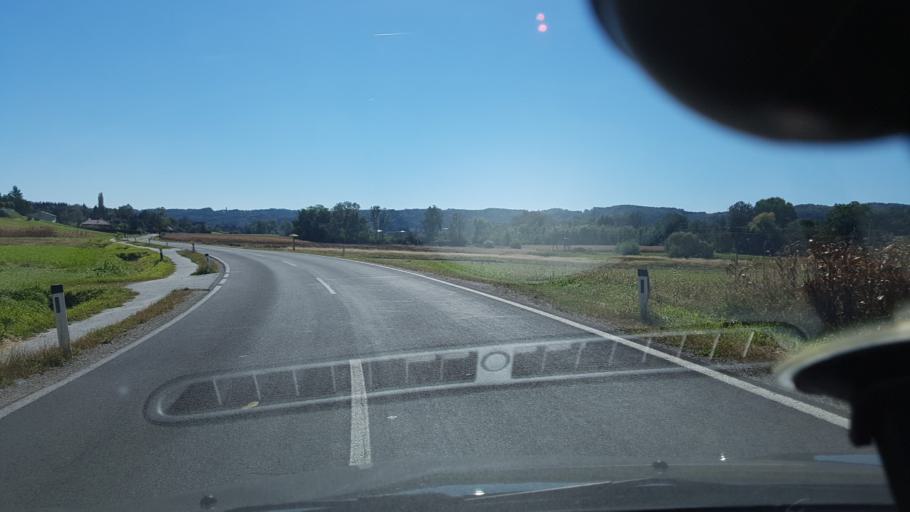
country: AT
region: Styria
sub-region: Politischer Bezirk Weiz
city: Sinabelkirchen
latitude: 47.1139
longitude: 15.8196
